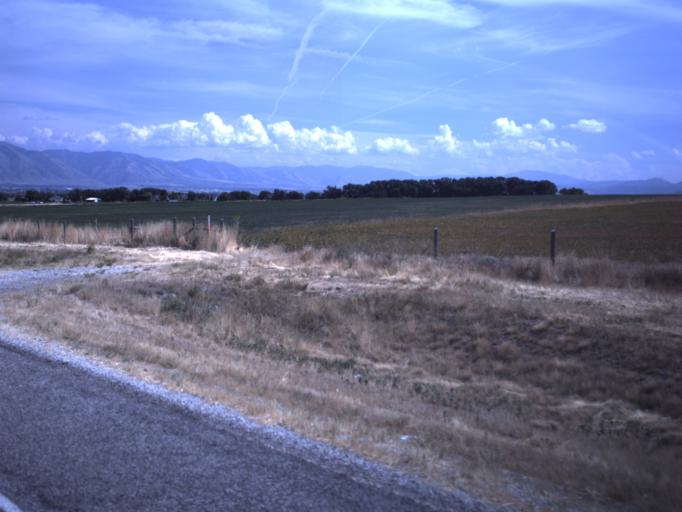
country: US
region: Utah
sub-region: Cache County
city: Mendon
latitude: 41.7551
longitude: -111.9979
